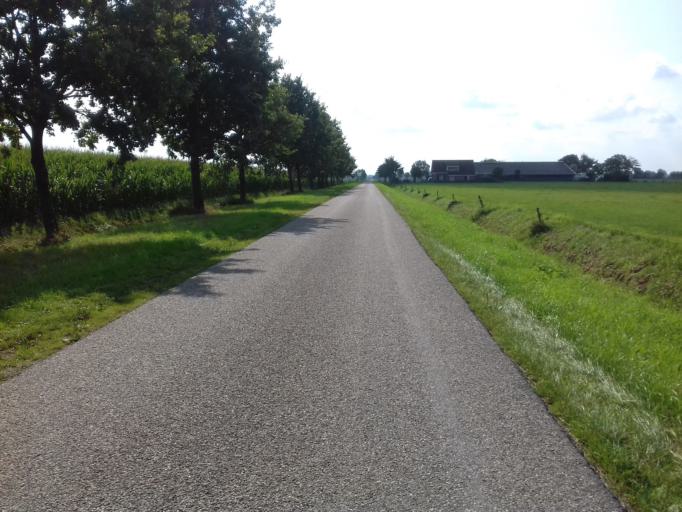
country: NL
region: Gelderland
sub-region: Gemeente Zaltbommel
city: Zaltbommel
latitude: 51.8676
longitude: 5.1852
